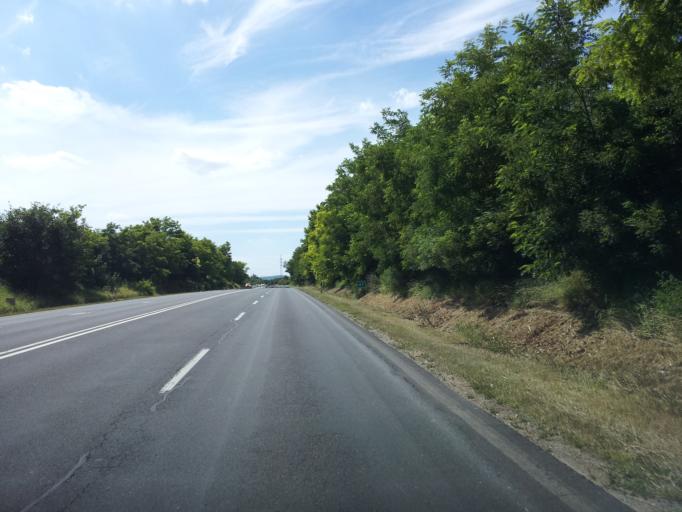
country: HU
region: Veszprem
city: Veszprem
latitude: 47.1017
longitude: 17.9515
